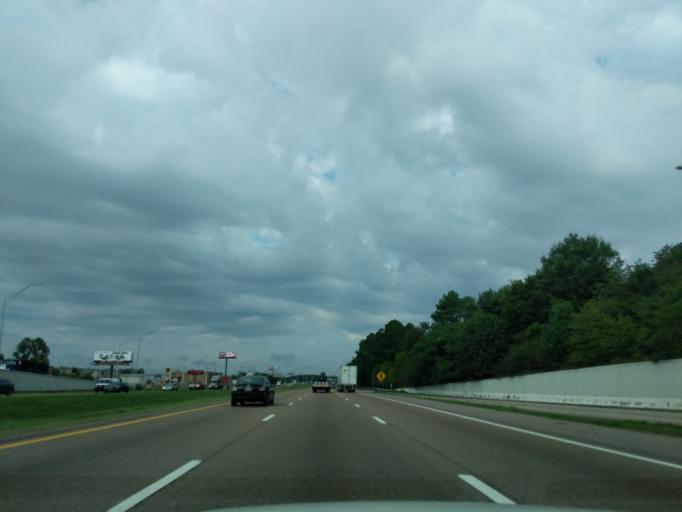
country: US
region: Tennessee
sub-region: Shelby County
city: New South Memphis
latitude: 35.0732
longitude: -90.0101
